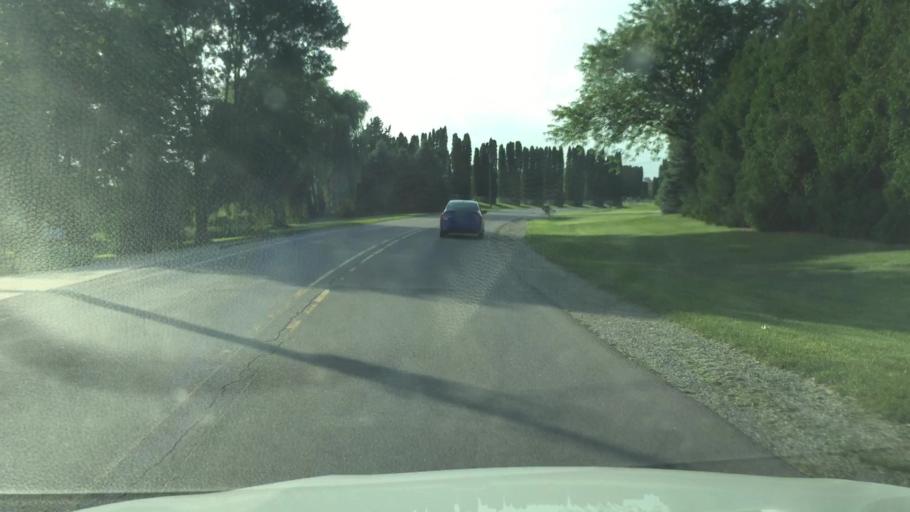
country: US
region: Iowa
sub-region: Linn County
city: Ely
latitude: 41.8419
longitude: -91.6453
